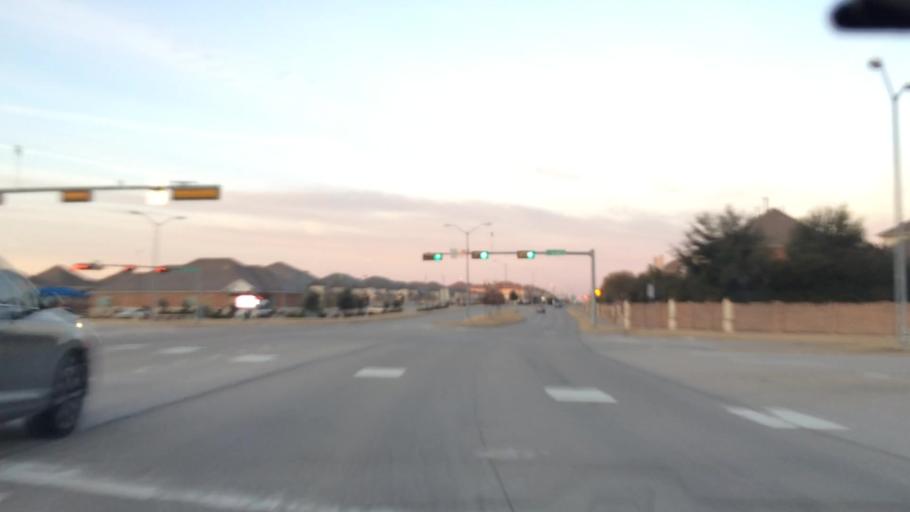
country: US
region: Texas
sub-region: Collin County
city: Frisco
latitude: 33.0943
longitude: -96.7916
